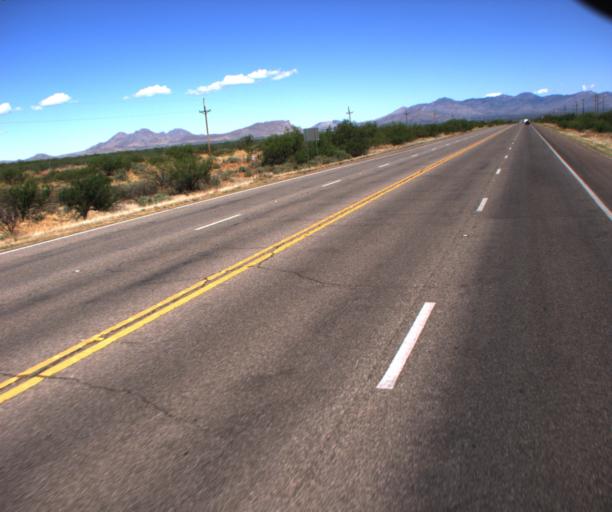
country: US
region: Arizona
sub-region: Cochise County
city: Huachuca City
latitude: 31.5956
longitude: -110.3251
